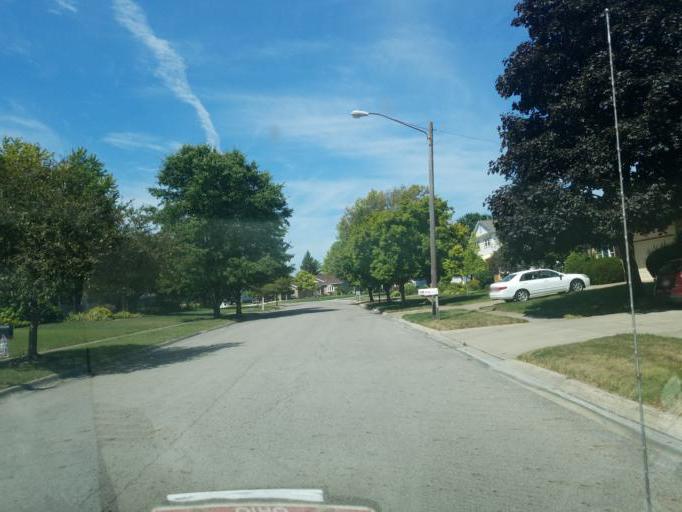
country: US
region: Ohio
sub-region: Franklin County
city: Grove City
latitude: 39.8738
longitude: -83.0727
